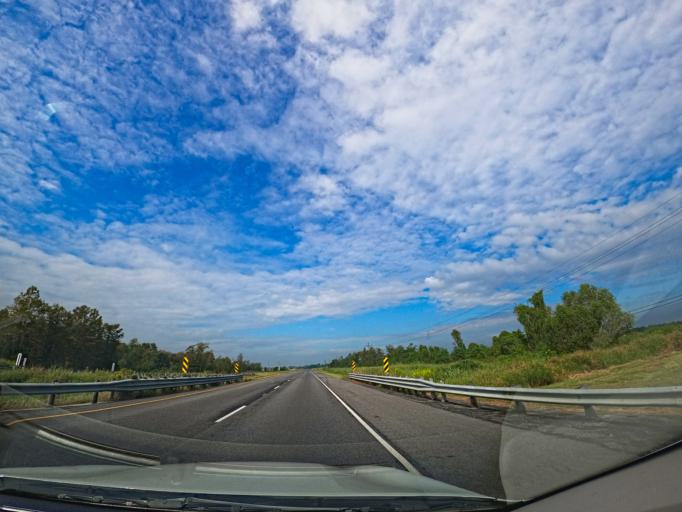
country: US
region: Louisiana
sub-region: Saint Mary Parish
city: Patterson
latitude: 29.6959
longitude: -91.3503
